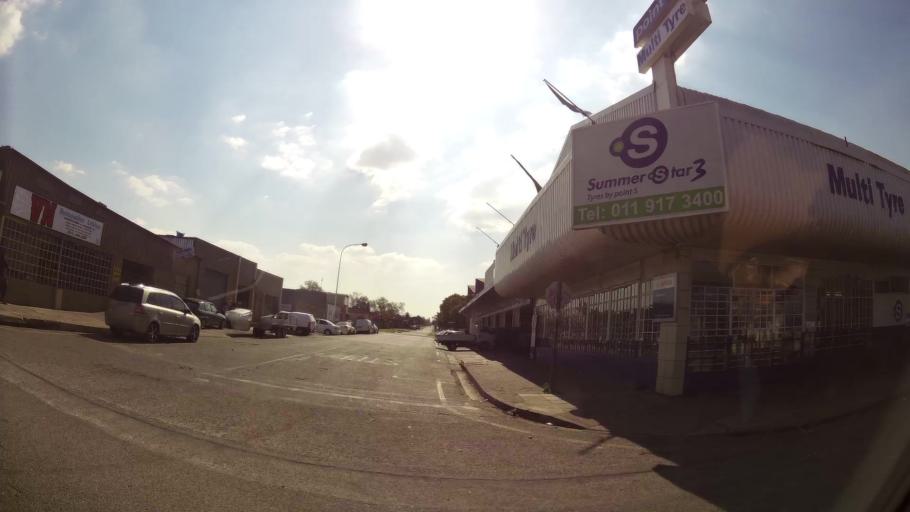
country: ZA
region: Gauteng
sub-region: Ekurhuleni Metropolitan Municipality
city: Boksburg
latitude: -26.2087
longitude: 28.2516
